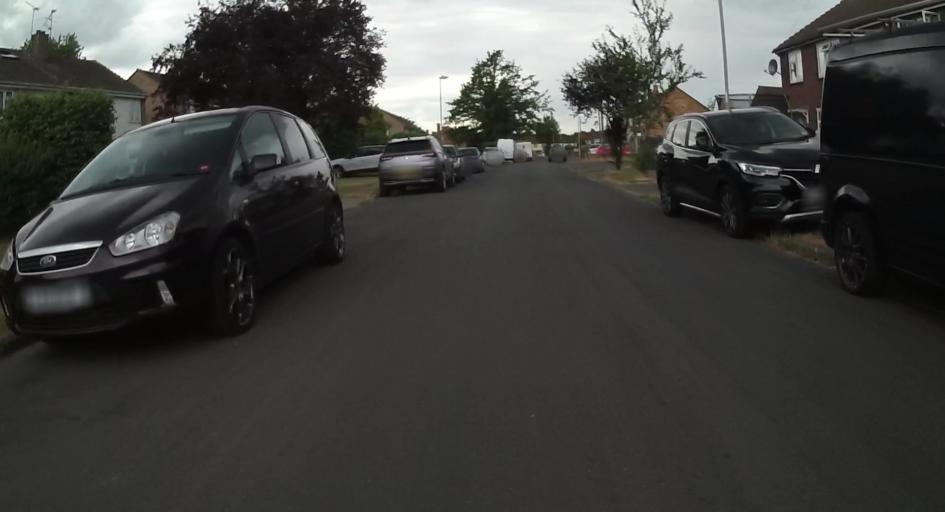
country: GB
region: England
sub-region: Surrey
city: Seale
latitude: 51.2376
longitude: -0.7379
